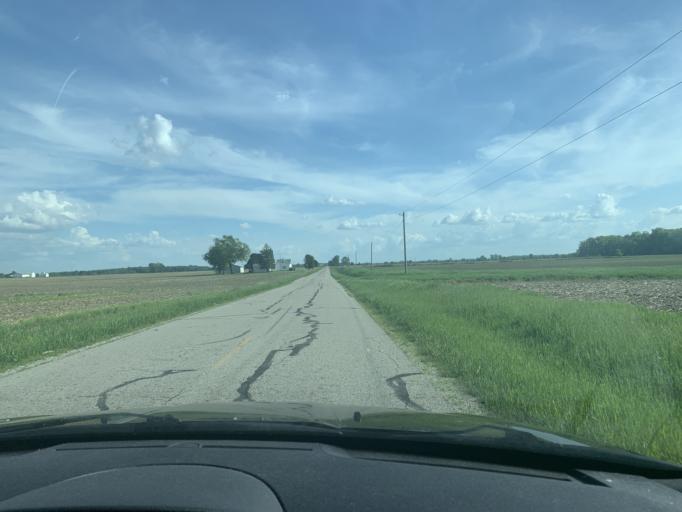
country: US
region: Ohio
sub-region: Logan County
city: De Graff
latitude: 40.2820
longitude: -84.0140
